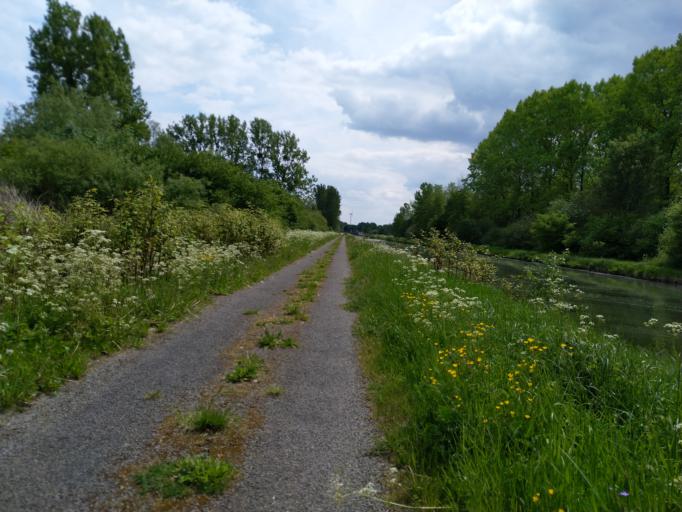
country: FR
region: Picardie
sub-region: Departement de l'Aisne
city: Wassigny
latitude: 50.0538
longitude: 3.6431
